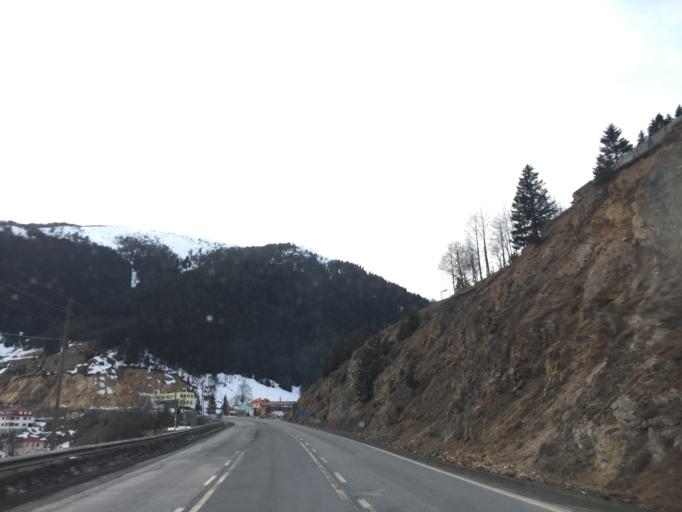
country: TR
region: Gumushane
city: Yaglidere
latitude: 40.6746
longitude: 39.4232
